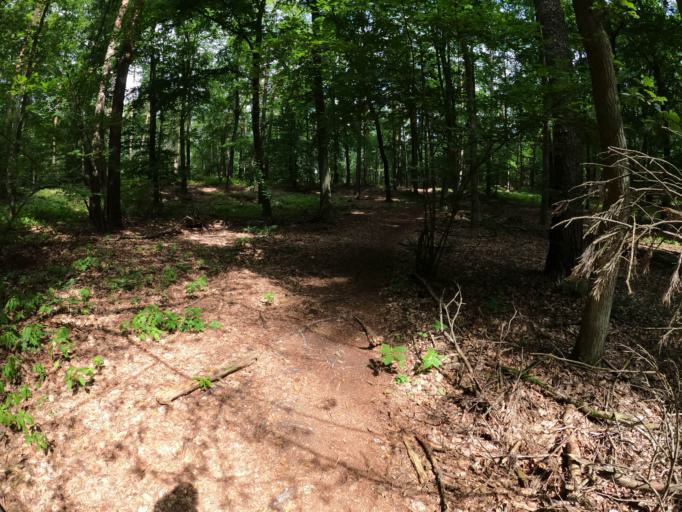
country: DE
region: Brandenburg
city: Angermunde
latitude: 53.0338
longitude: 13.9395
